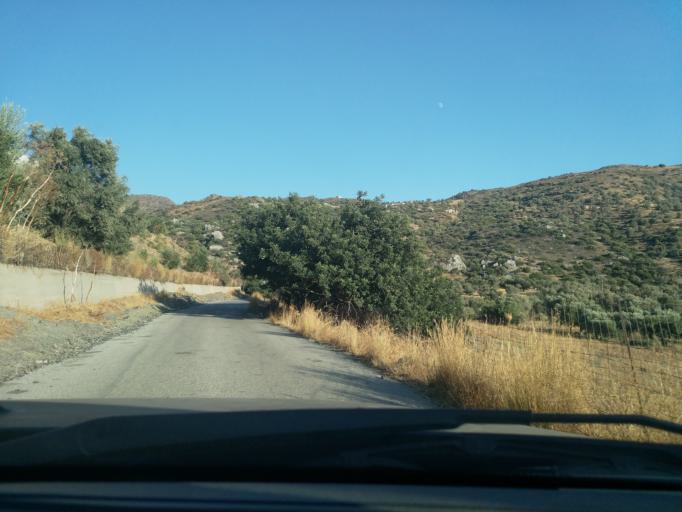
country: GR
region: Crete
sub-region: Nomos Rethymnis
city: Agia Galini
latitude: 35.1164
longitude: 24.5640
